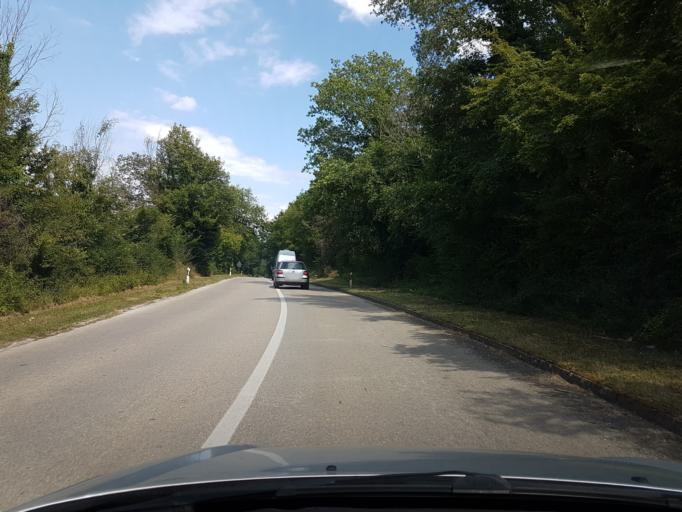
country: HR
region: Istarska
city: Vrsar
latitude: 45.1529
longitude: 13.6431
